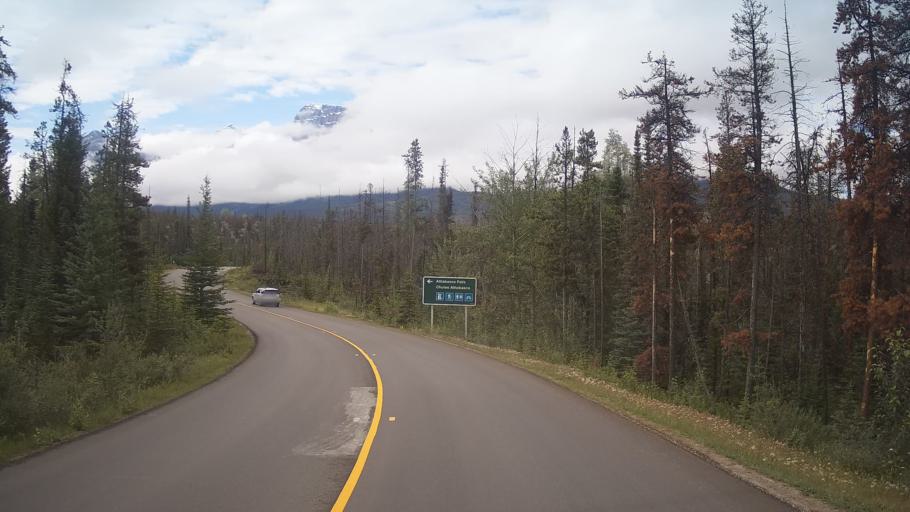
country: CA
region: Alberta
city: Jasper Park Lodge
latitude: 52.6680
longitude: -117.8836
